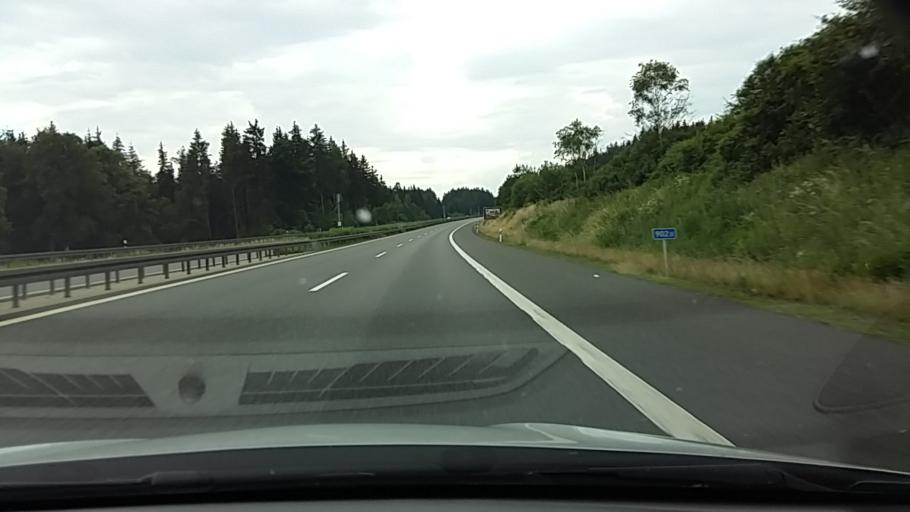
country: DE
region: Bavaria
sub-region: Upper Palatinate
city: Pleystein
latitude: 49.6296
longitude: 12.4474
